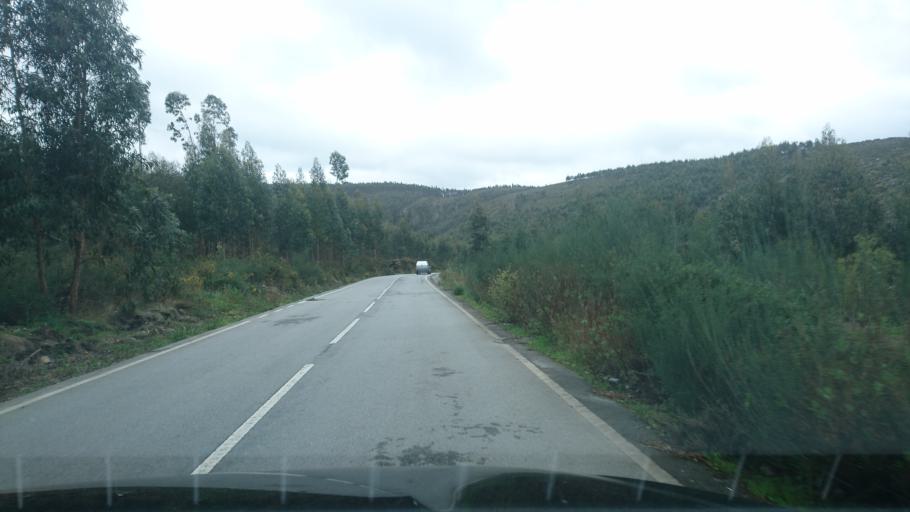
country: PT
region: Porto
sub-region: Paredes
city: Recarei
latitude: 41.1327
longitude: -8.4002
